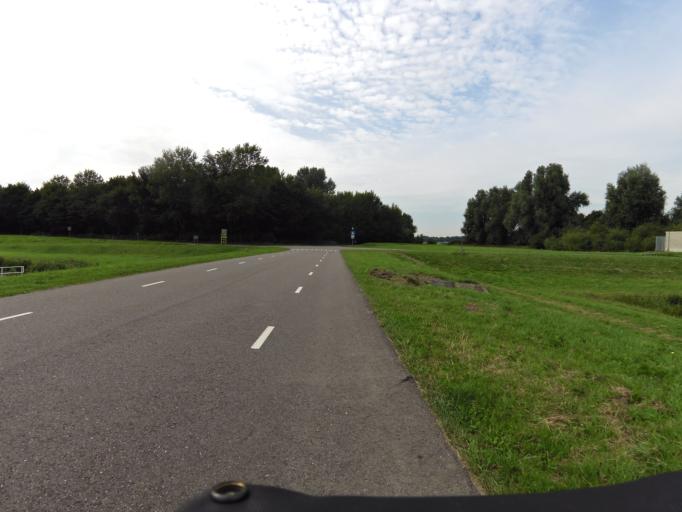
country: NL
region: South Holland
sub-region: Gemeente Maassluis
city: Maassluis
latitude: 51.8701
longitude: 4.2322
